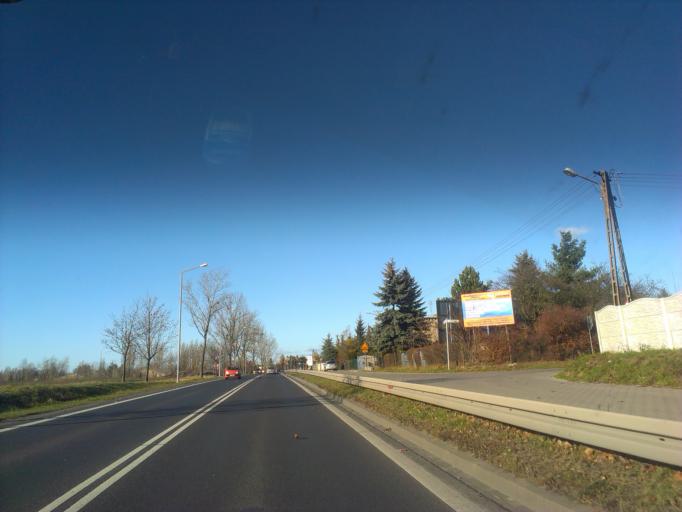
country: PL
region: Greater Poland Voivodeship
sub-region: Powiat poznanski
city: Zlotniki
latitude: 52.4894
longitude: 16.8495
